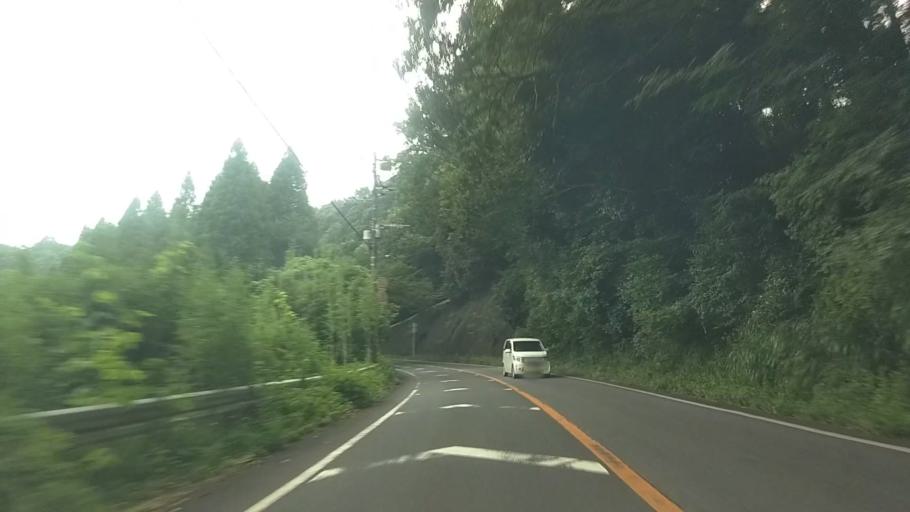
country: JP
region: Chiba
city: Kawaguchi
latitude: 35.2428
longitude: 140.0759
